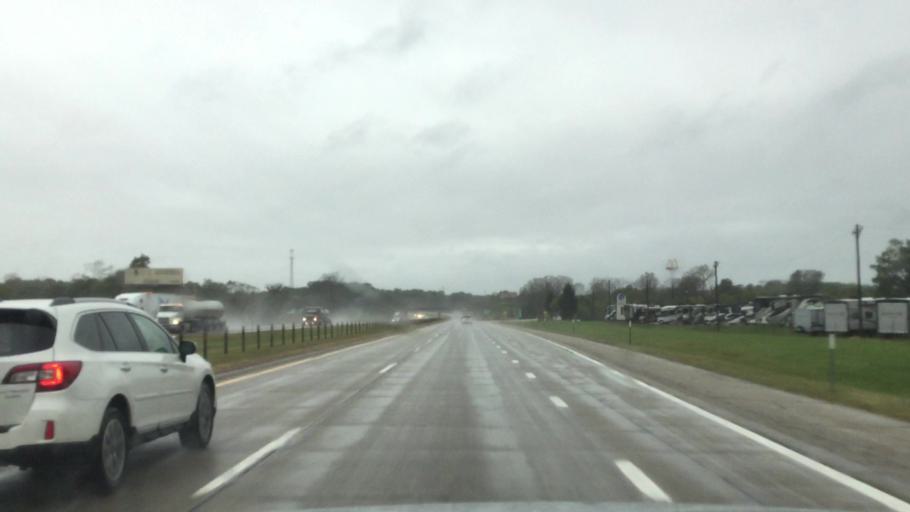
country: US
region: Michigan
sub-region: Berrien County
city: Coloma
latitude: 42.1764
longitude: -86.2981
